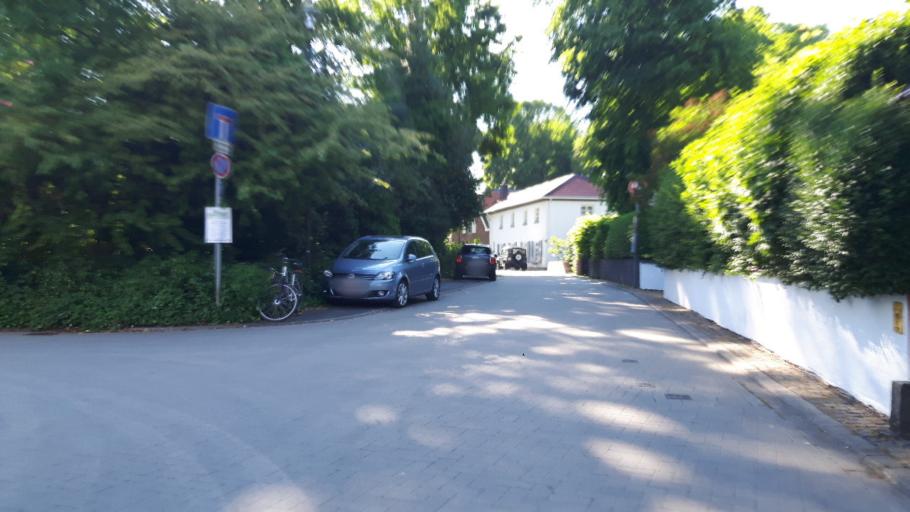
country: DE
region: North Rhine-Westphalia
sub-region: Regierungsbezirk Dusseldorf
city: Dusseldorf
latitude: 51.3027
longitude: 6.7570
